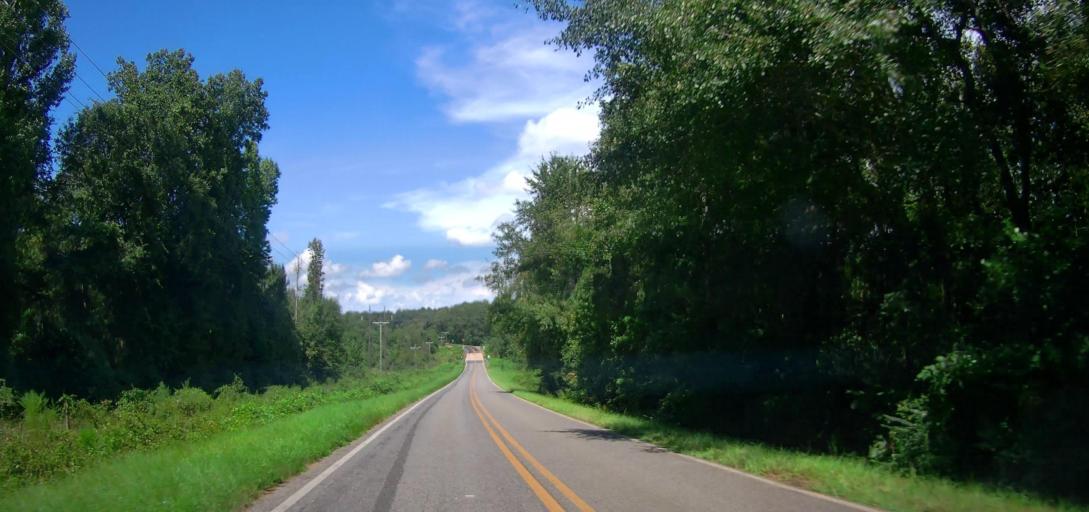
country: US
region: Georgia
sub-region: Macon County
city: Marshallville
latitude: 32.4758
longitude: -83.8666
